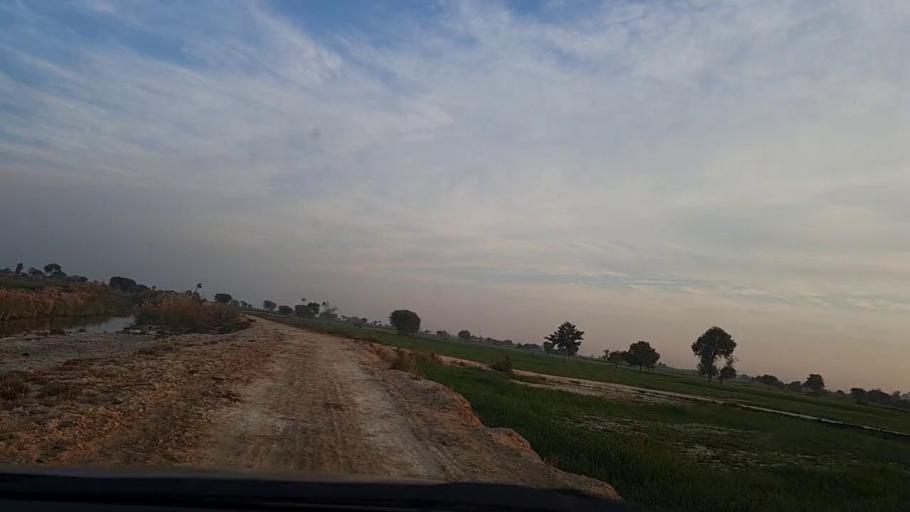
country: PK
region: Sindh
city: Sakrand
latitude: 26.1729
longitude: 68.3460
